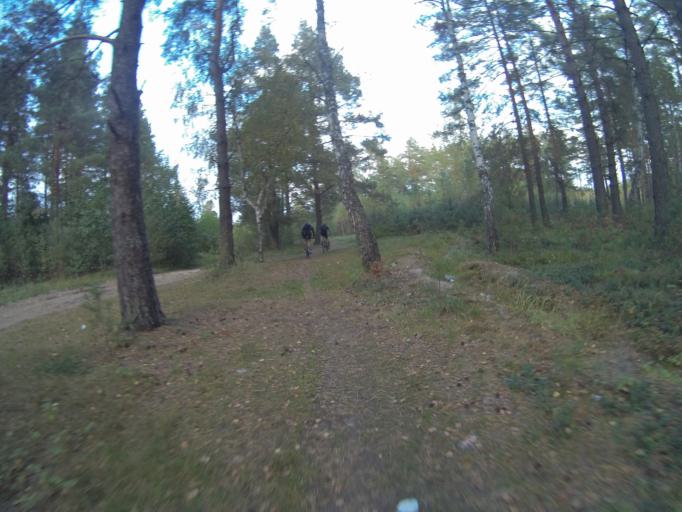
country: RU
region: Vladimir
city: Sobinka
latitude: 55.9750
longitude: 40.0077
